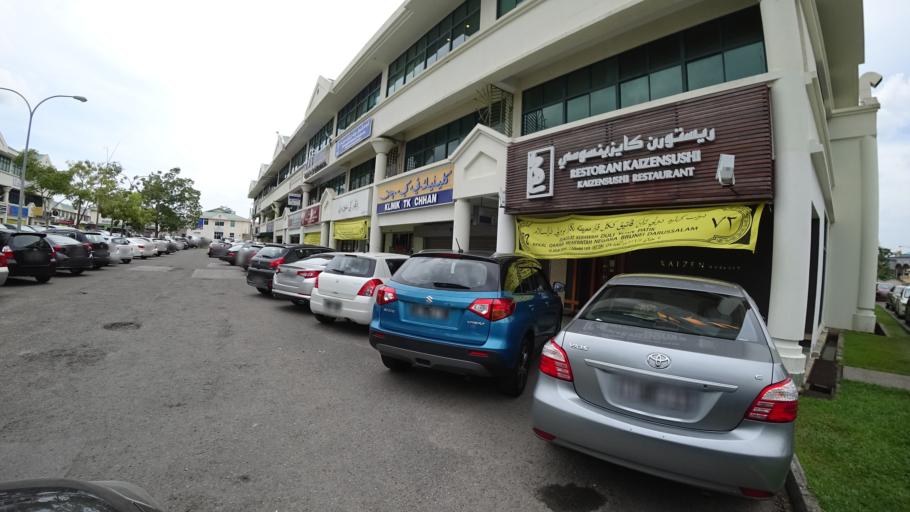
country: BN
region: Brunei and Muara
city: Bandar Seri Begawan
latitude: 4.8957
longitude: 114.9210
